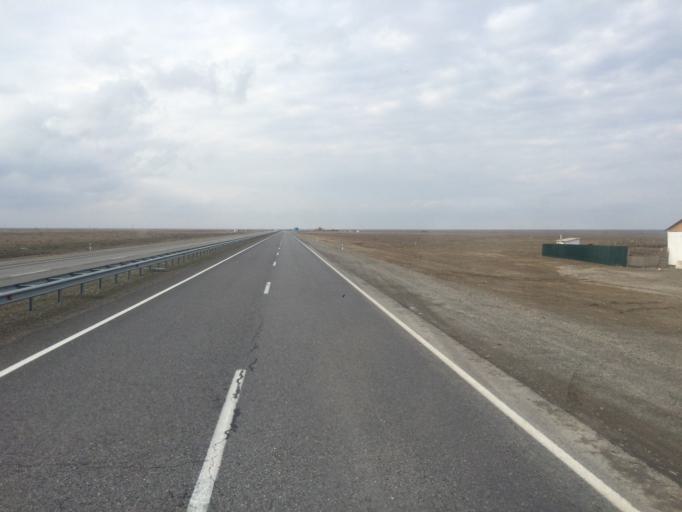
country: KZ
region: Ongtustik Qazaqstan
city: Turkestan
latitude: 43.5274
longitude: 67.7903
